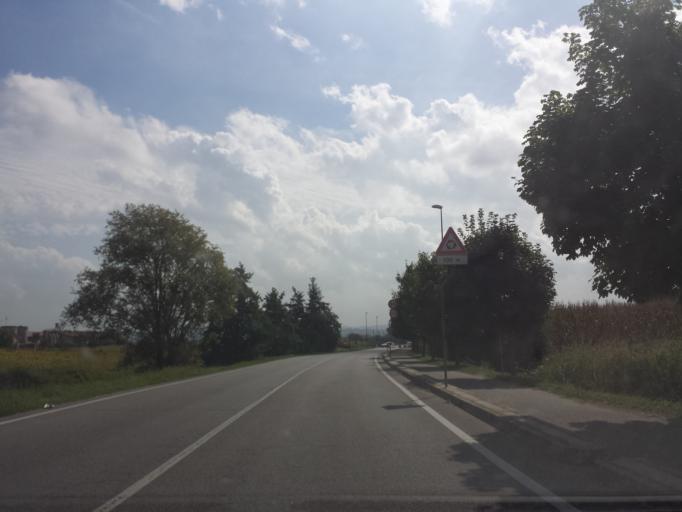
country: IT
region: Veneto
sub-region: Provincia di Vicenza
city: Creazzo
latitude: 45.5386
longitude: 11.4904
